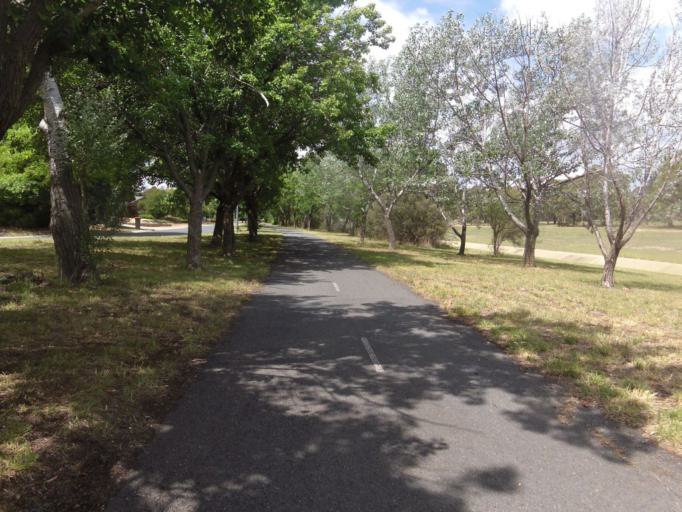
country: AU
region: Australian Capital Territory
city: Macarthur
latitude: -35.4174
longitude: 149.1108
